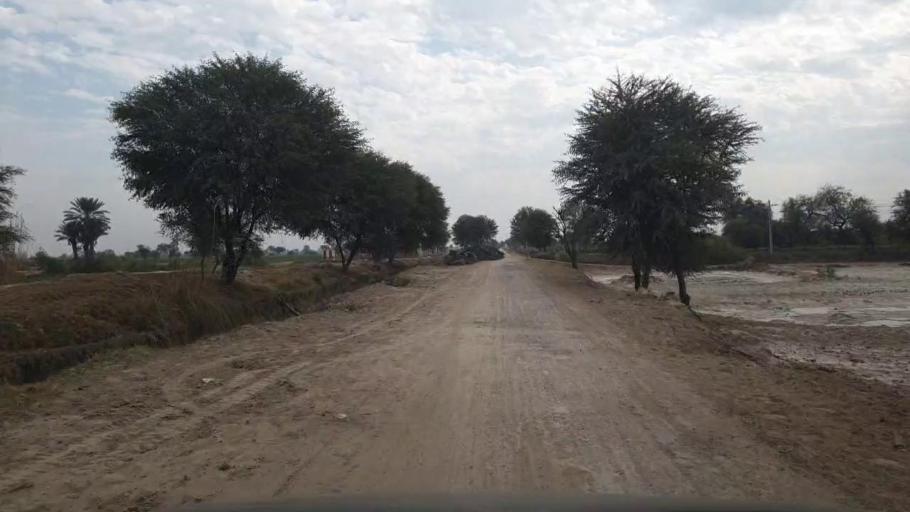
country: PK
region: Sindh
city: Sakrand
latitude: 26.0239
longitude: 68.4277
